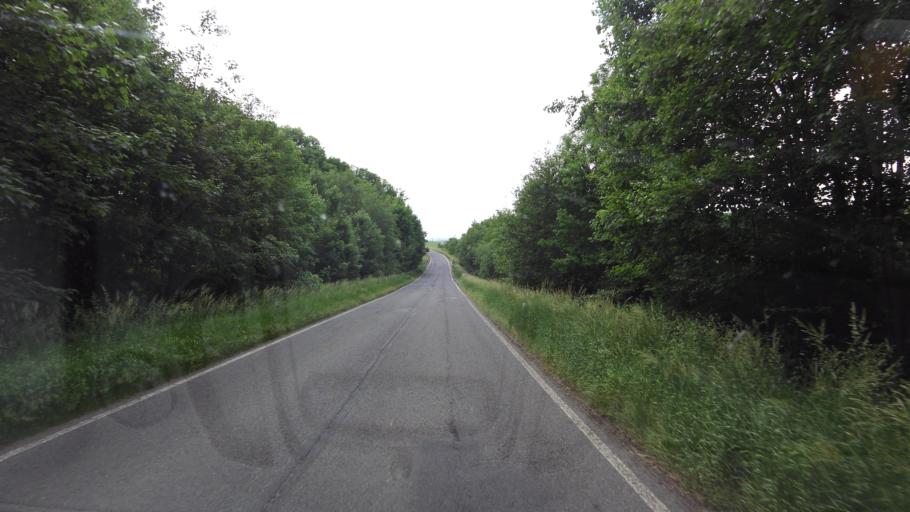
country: CZ
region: Plzensky
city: Prestice
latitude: 49.5898
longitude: 13.3776
